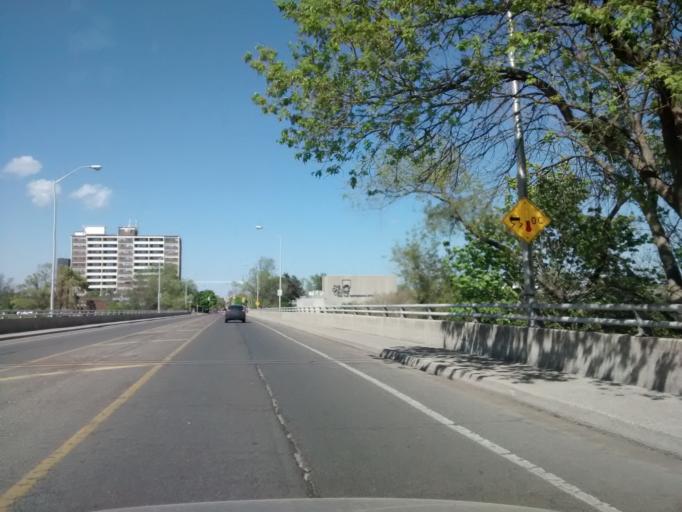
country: CA
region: Ontario
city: Oakville
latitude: 43.4431
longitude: -79.6736
